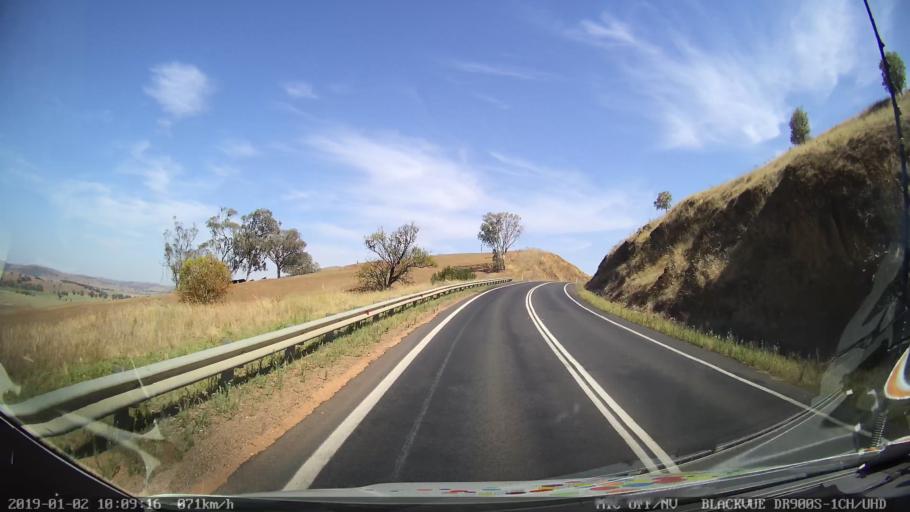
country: AU
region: New South Wales
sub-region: Gundagai
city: Gundagai
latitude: -35.1184
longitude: 148.0999
